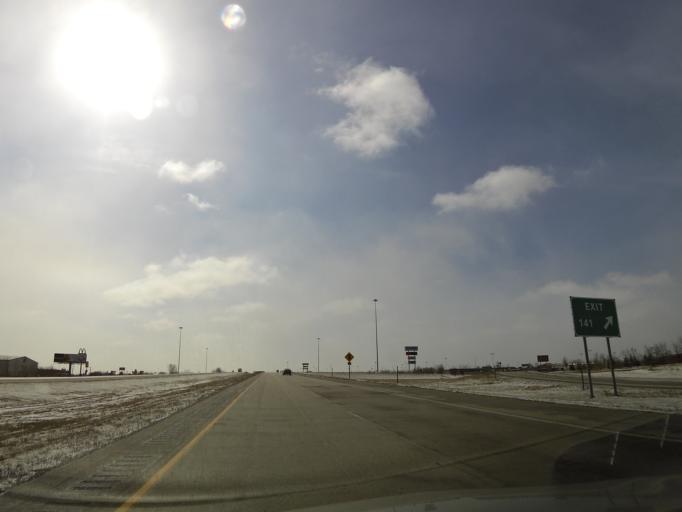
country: US
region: North Dakota
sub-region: Grand Forks County
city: Grand Forks
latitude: 47.9374
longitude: -97.0938
